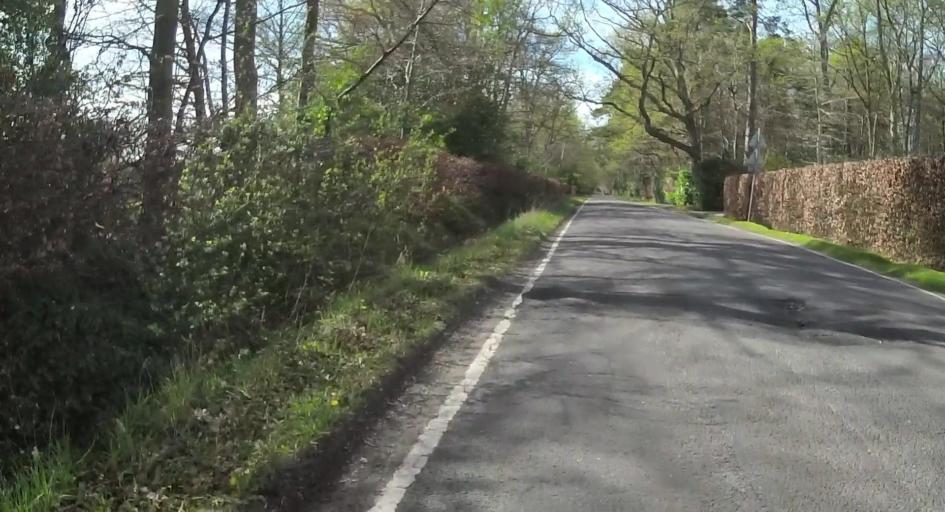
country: GB
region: England
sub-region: Surrey
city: Farnham
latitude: 51.1803
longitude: -0.8122
